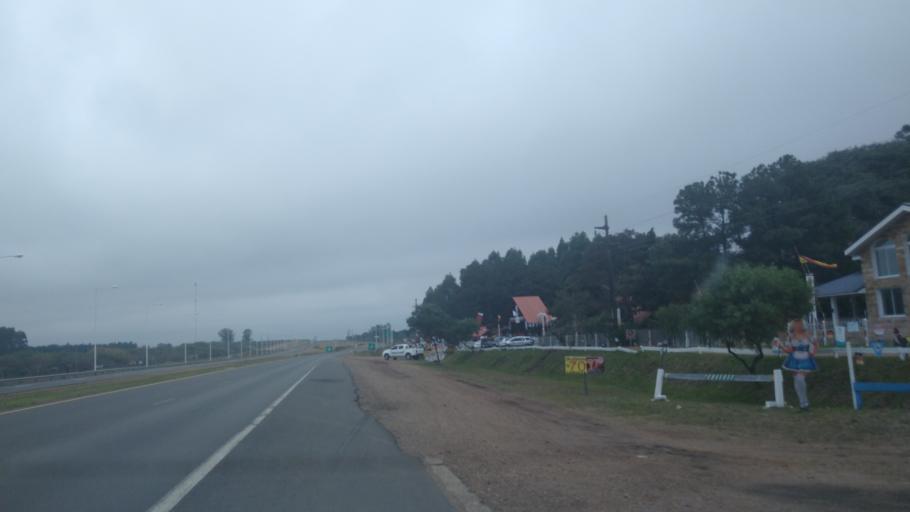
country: AR
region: Entre Rios
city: Santa Ana
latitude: -30.8943
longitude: -58.0437
